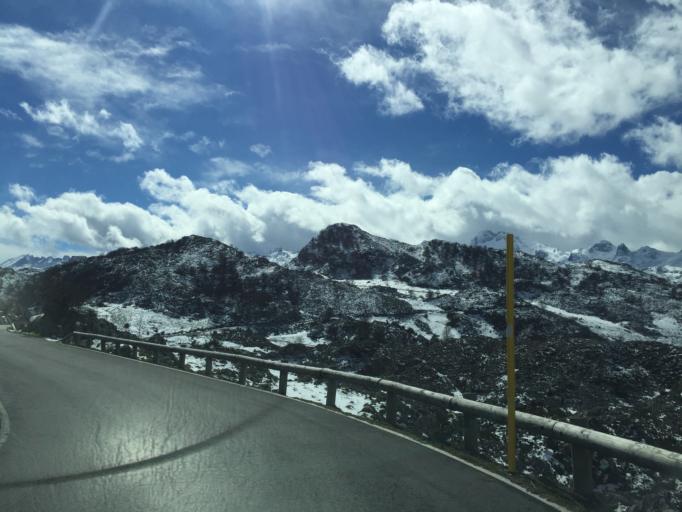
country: ES
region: Asturias
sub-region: Province of Asturias
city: Amieva
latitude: 43.2842
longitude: -5.0082
